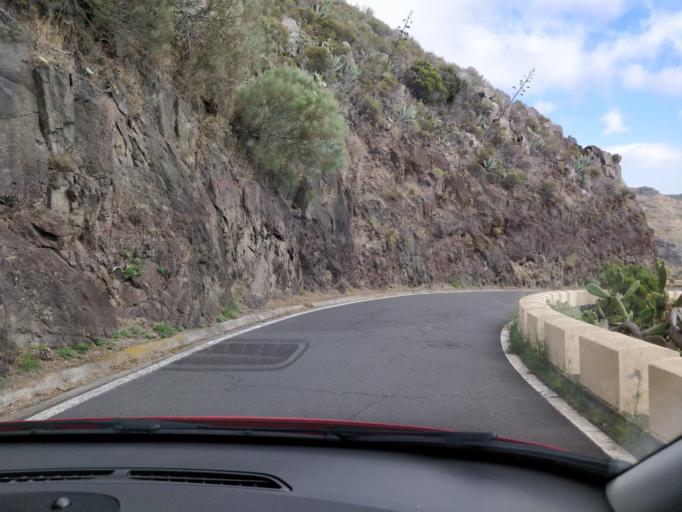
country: ES
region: Canary Islands
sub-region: Provincia de Santa Cruz de Tenerife
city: Tanque
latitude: 28.3232
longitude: -16.8571
